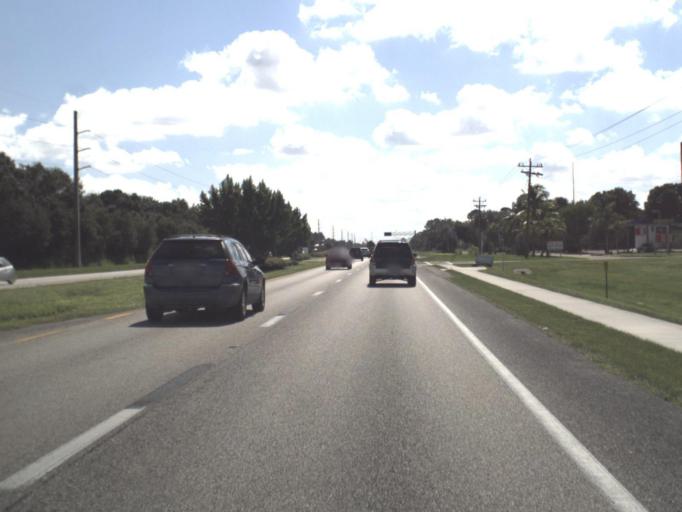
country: US
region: Florida
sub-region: Lee County
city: Palmona Park
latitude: 26.6766
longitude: -81.8985
